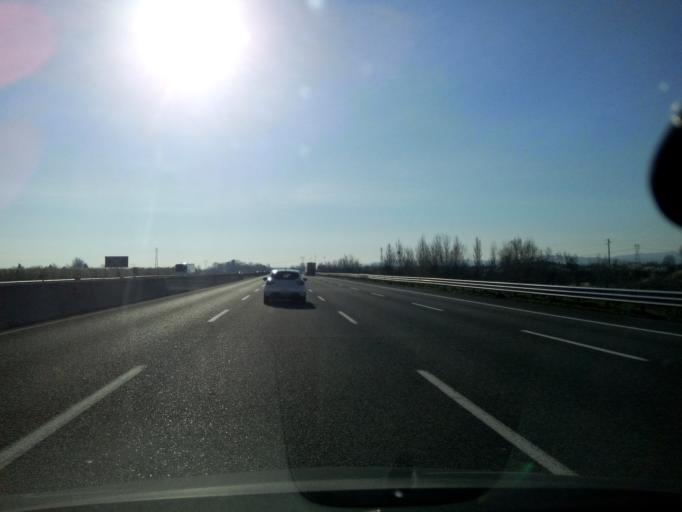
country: IT
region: Emilia-Romagna
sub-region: Provincia di Modena
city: San Cesario sul Panaro
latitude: 44.5632
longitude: 11.0477
